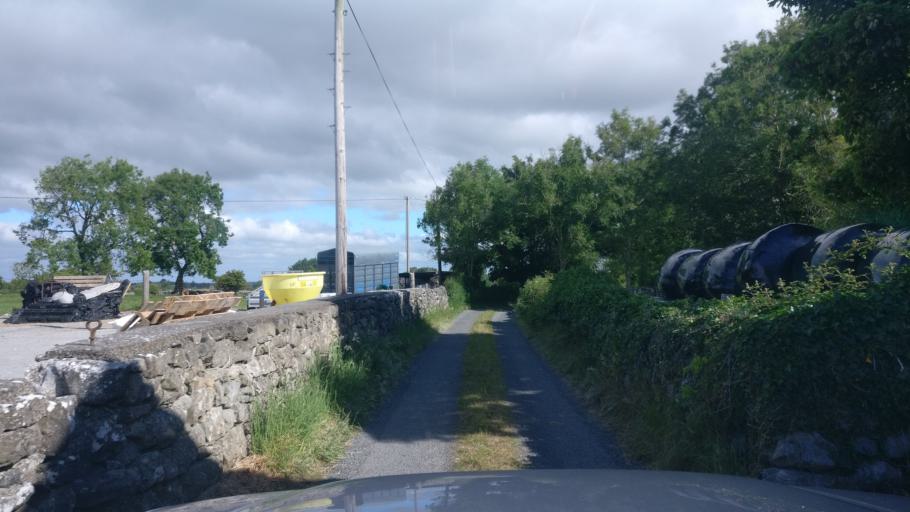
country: IE
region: Connaught
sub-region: County Galway
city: Loughrea
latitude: 53.2324
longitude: -8.6002
